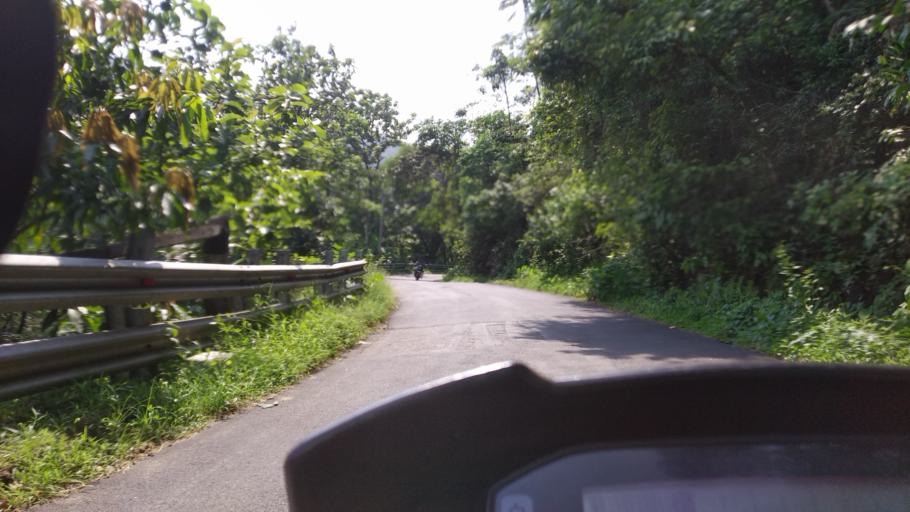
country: IN
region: Kerala
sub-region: Kottayam
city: Erattupetta
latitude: 9.6922
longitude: 76.8409
